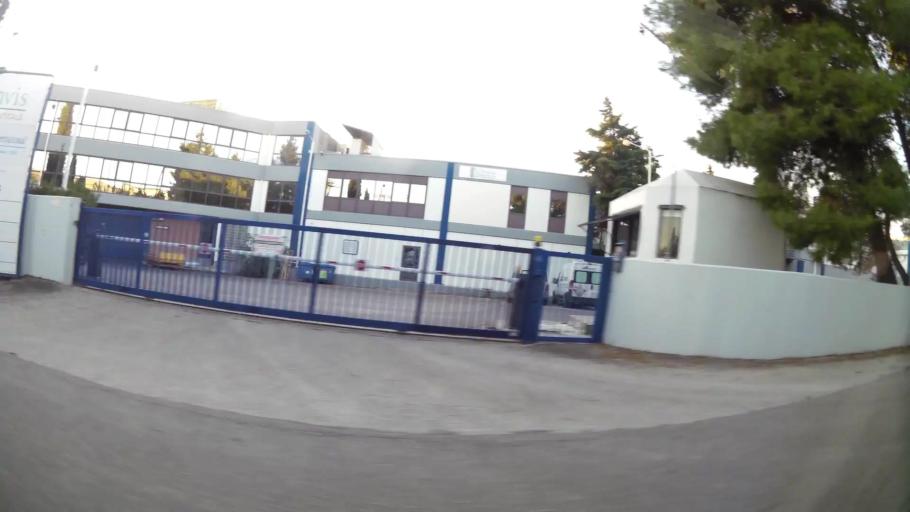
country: GR
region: Attica
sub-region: Nomarchia Anatolikis Attikis
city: Kryoneri
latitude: 38.1380
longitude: 23.8368
